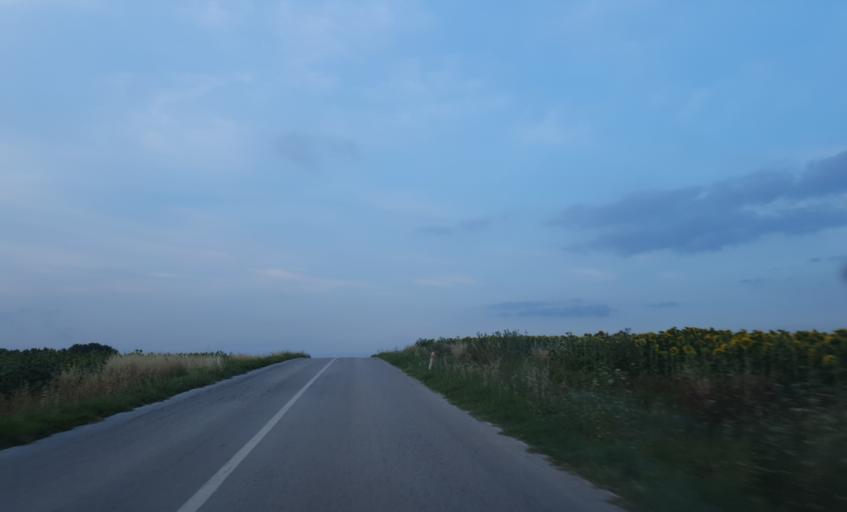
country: TR
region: Tekirdag
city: Beyazkoy
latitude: 41.3964
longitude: 27.6340
